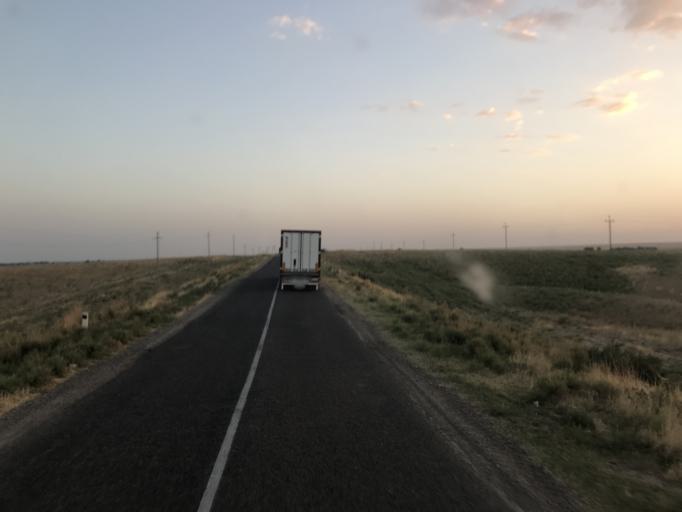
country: UZ
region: Toshkent
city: Amir Timur
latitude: 41.3349
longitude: 68.6894
